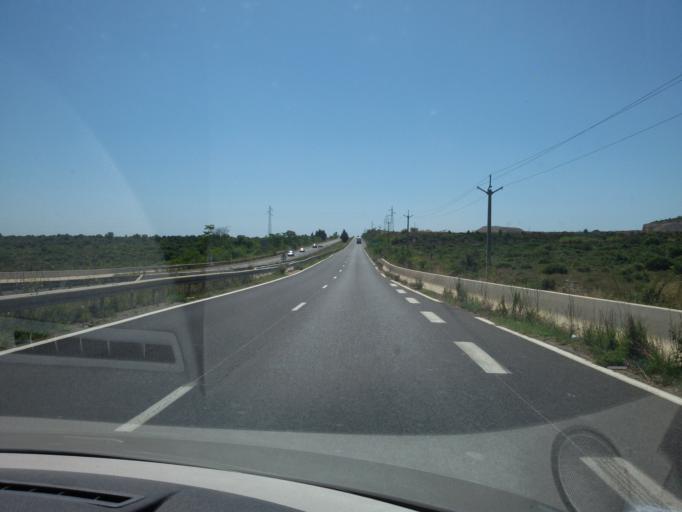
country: FR
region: Languedoc-Roussillon
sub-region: Departement de l'Herault
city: Saint-Jean-de-Vedas
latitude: 43.5435
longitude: 3.8229
